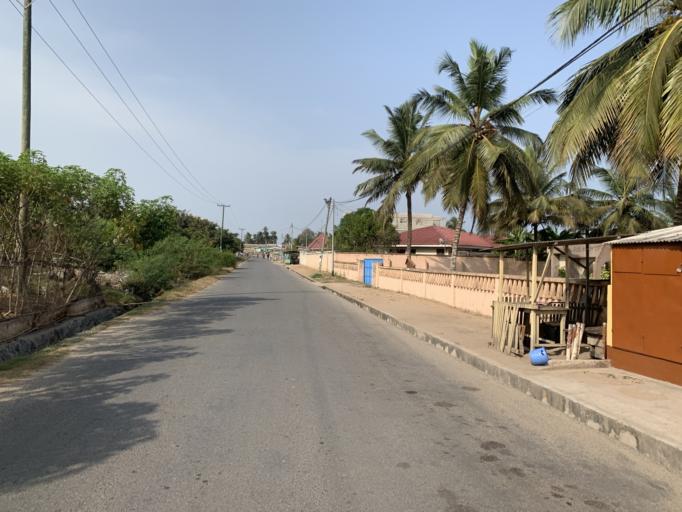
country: GH
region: Central
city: Winneba
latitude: 5.3336
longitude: -0.6268
